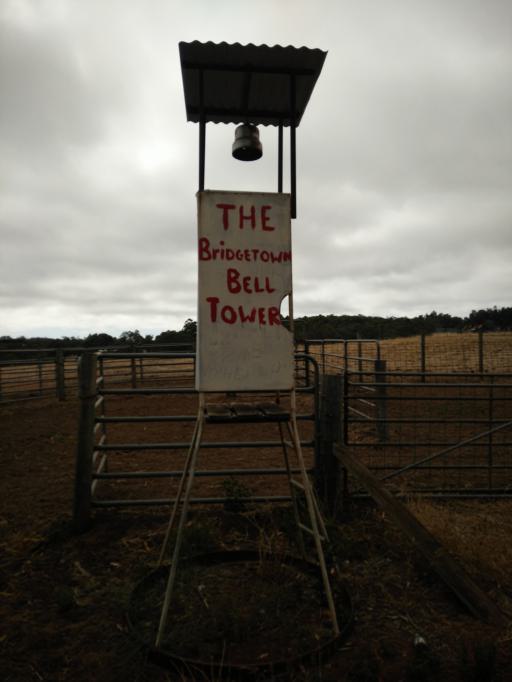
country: AU
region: Western Australia
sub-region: Bridgetown-Greenbushes
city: Bridgetown
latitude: -33.9530
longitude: 116.1699
